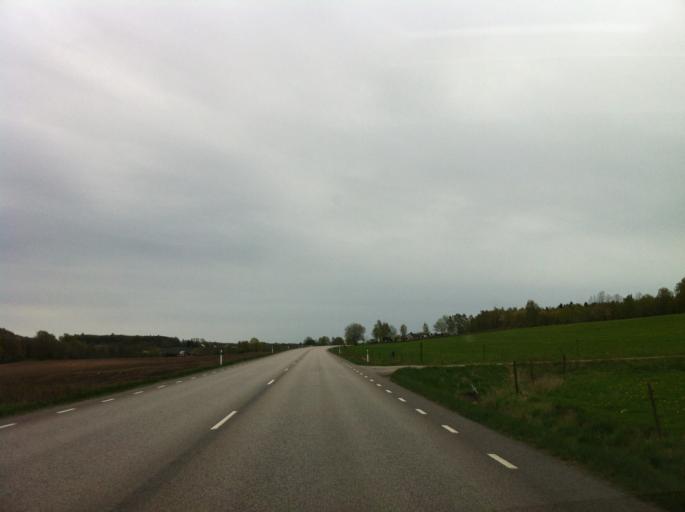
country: SE
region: Halland
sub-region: Falkenbergs Kommun
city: Falkenberg
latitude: 56.9777
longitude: 12.5774
